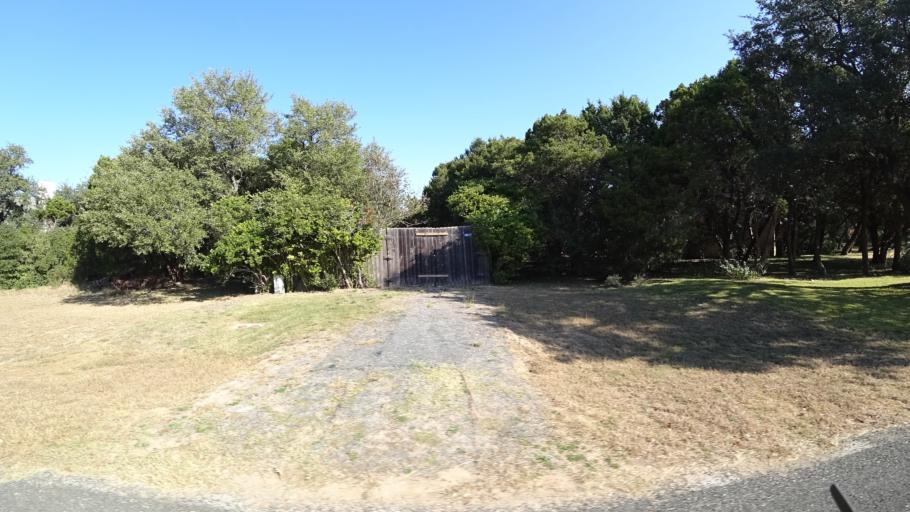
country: US
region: Texas
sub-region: Williamson County
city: Anderson Mill
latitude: 30.3771
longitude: -97.8201
